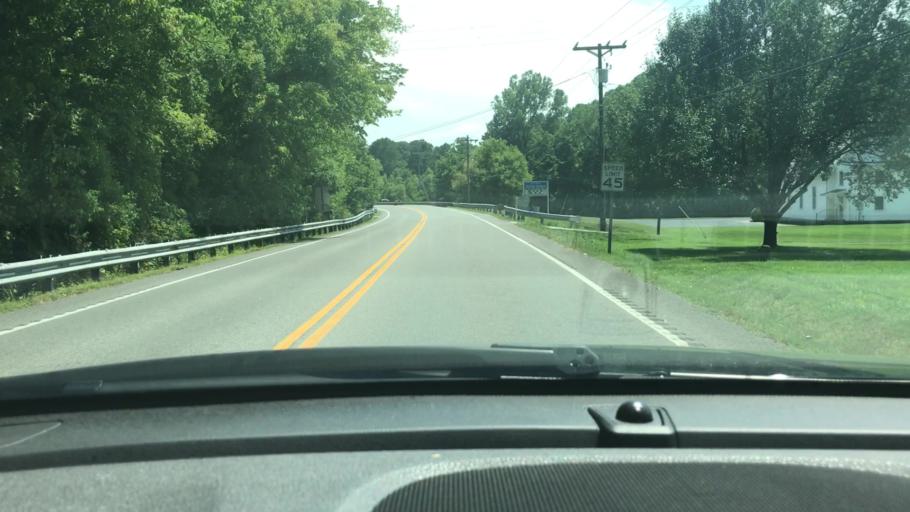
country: US
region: Tennessee
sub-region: Sumner County
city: Shackle Island
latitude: 36.4083
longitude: -86.6343
